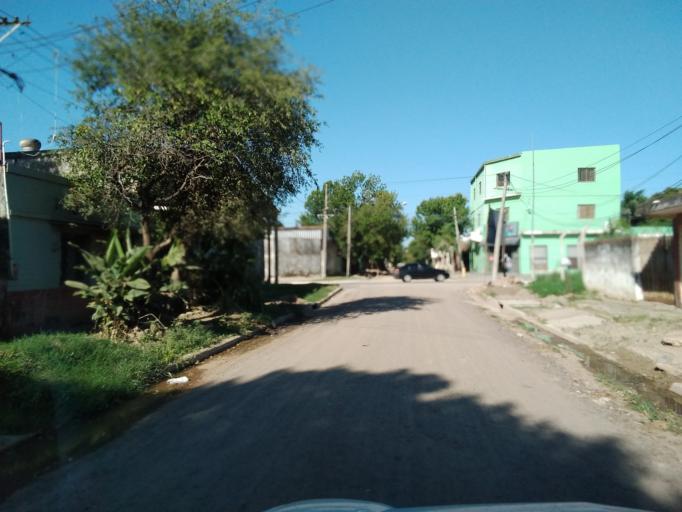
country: AR
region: Corrientes
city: Corrientes
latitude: -27.4841
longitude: -58.8085
